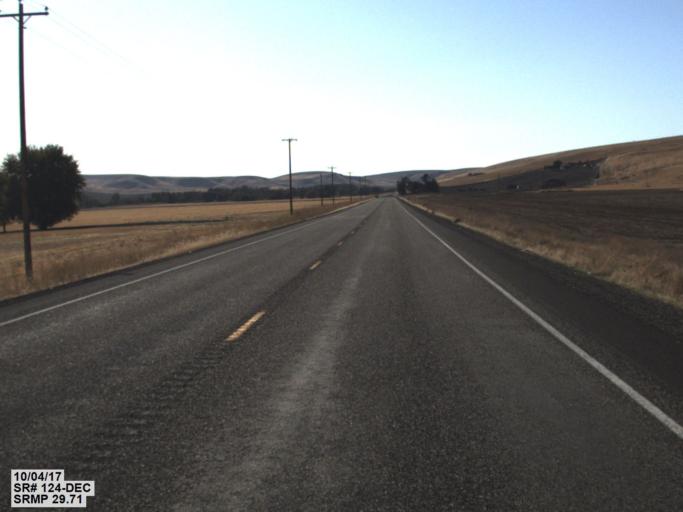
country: US
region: Washington
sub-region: Walla Walla County
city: Garrett
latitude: 46.2966
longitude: -118.4426
